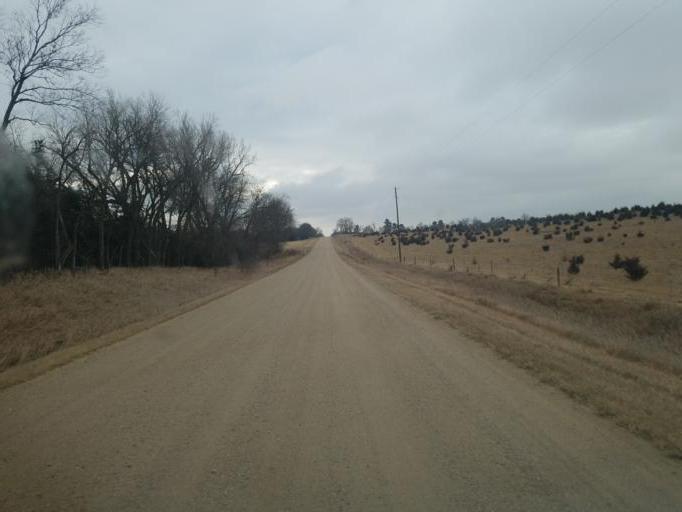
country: US
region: Nebraska
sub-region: Pierce County
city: Plainview
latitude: 42.4083
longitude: -97.7960
